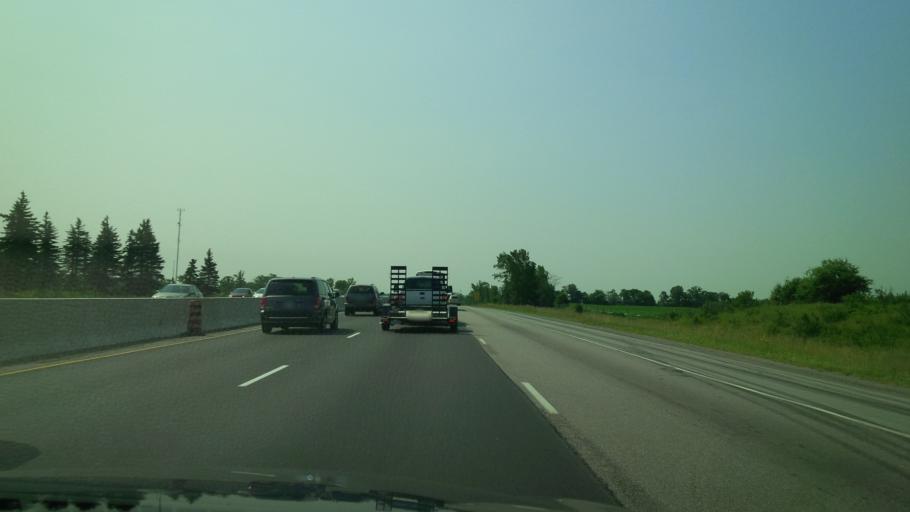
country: CA
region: Ontario
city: Bradford West Gwillimbury
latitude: 44.0853
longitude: -79.6274
